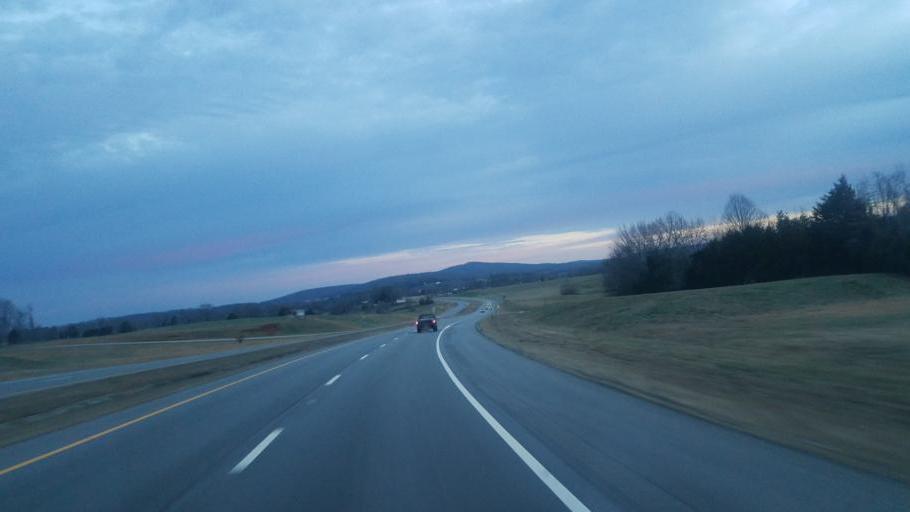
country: US
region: Tennessee
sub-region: Van Buren County
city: Spencer
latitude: 35.7974
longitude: -85.4604
